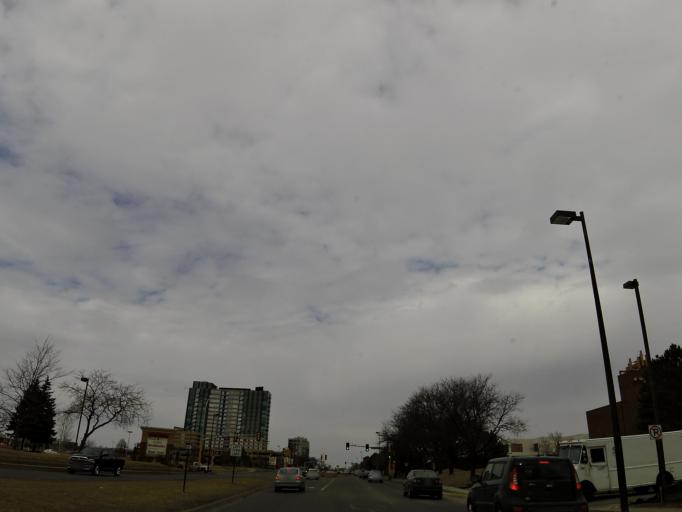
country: US
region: Minnesota
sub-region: Hennepin County
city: Edina
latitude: 44.8736
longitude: -93.3211
